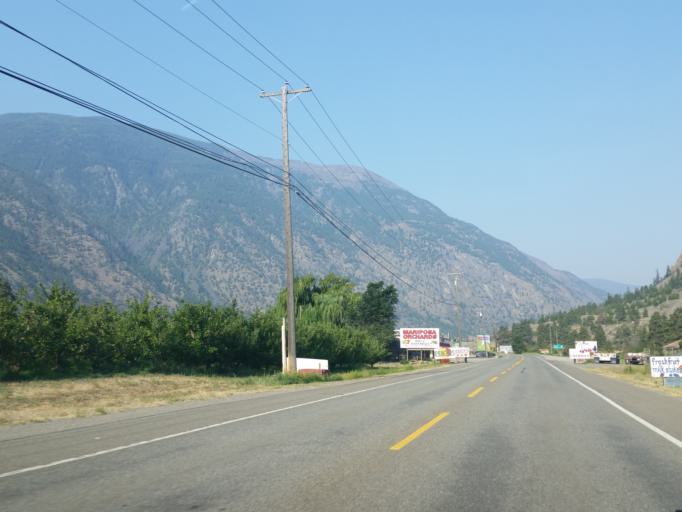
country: CA
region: British Columbia
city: Oliver
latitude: 49.2053
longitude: -119.8527
